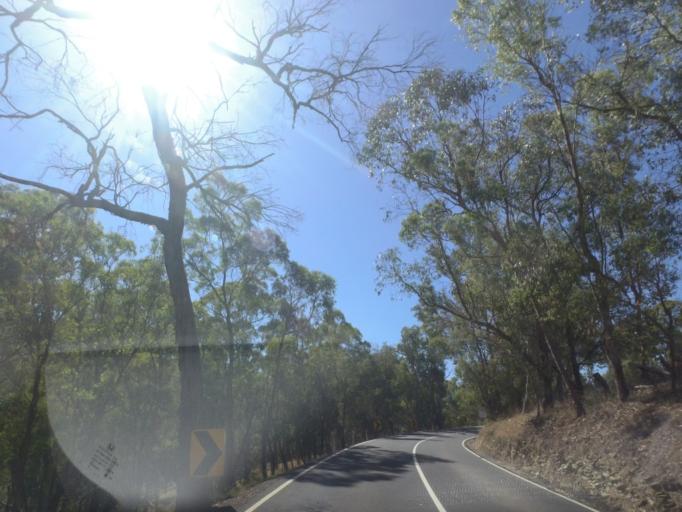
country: AU
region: Victoria
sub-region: Manningham
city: Warrandyte
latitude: -37.7533
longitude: 145.2560
